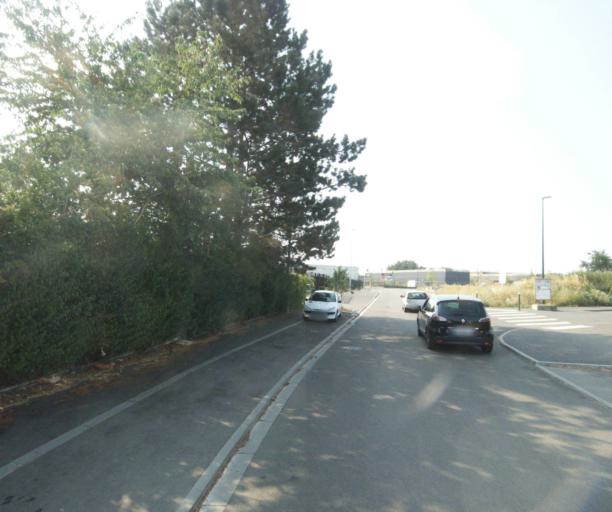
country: FR
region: Nord-Pas-de-Calais
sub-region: Departement du Nord
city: Neuville-en-Ferrain
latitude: 50.7394
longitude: 3.1475
